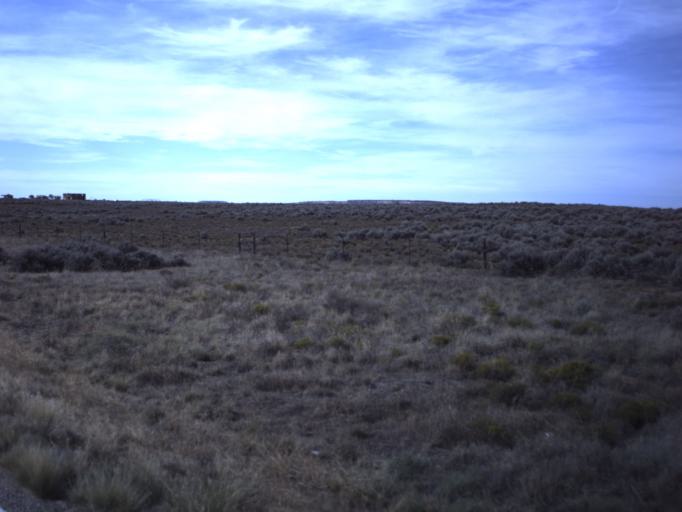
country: US
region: Utah
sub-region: San Juan County
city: Blanding
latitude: 37.4077
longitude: -109.3361
